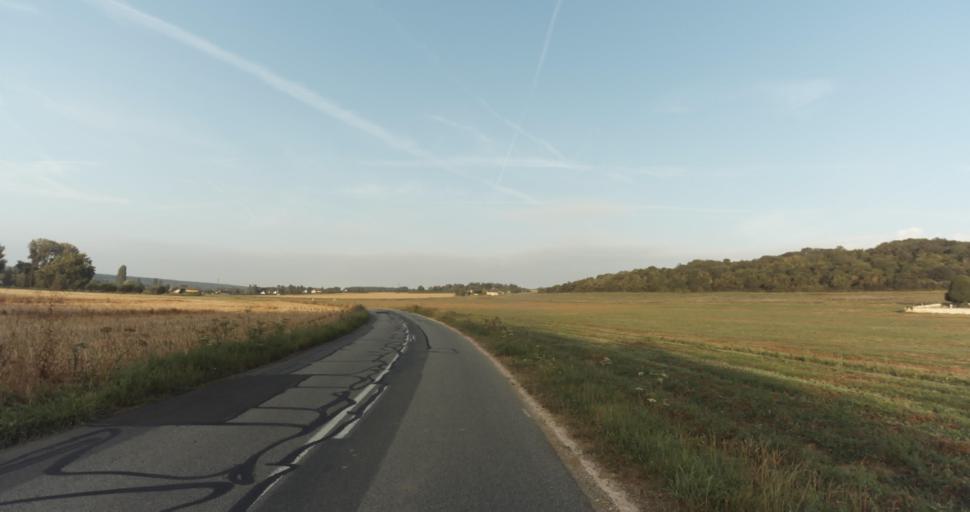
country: FR
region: Haute-Normandie
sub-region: Departement de l'Eure
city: Marcilly-sur-Eure
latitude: 48.7793
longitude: 1.3408
